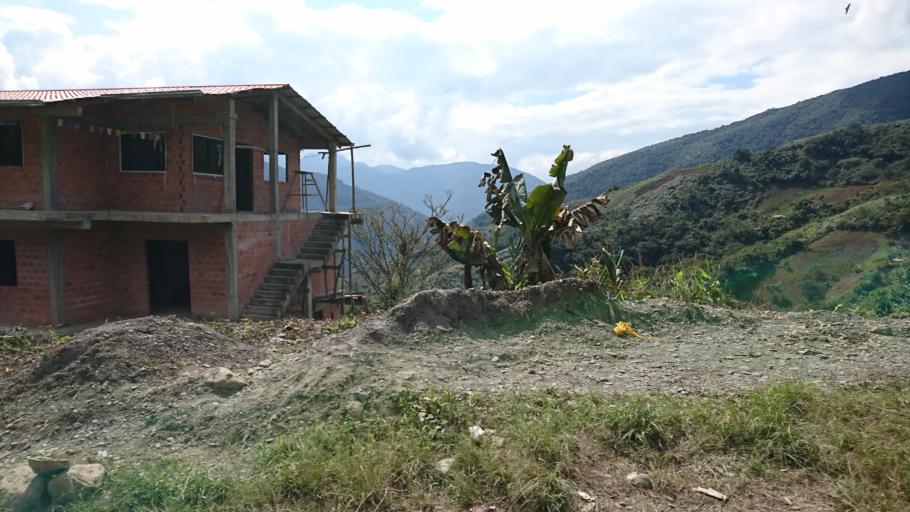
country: BO
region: La Paz
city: Coroico
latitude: -16.1280
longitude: -67.7546
